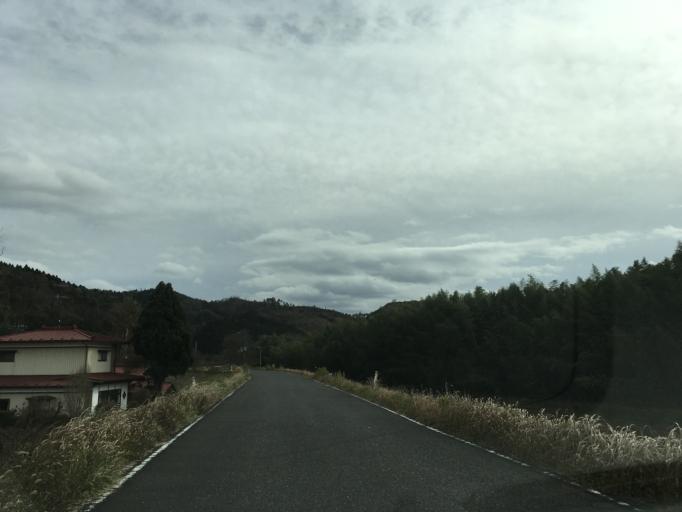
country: JP
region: Iwate
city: Ichinoseki
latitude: 38.7552
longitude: 141.2800
